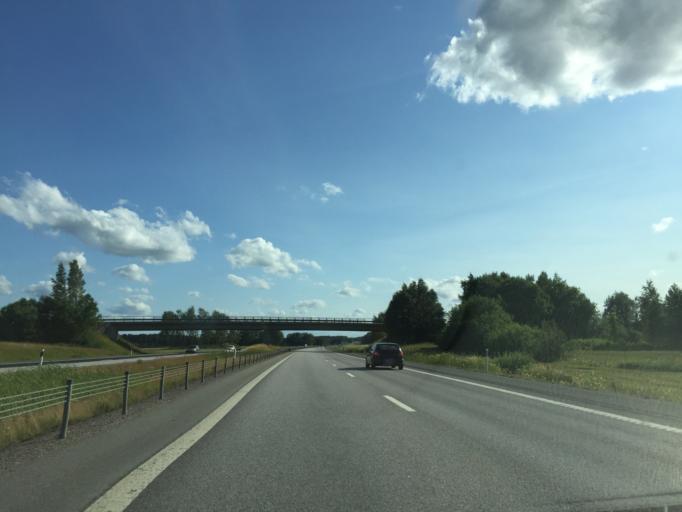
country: SE
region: OErebro
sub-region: Kumla Kommun
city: Kumla
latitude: 59.1538
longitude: 15.1006
